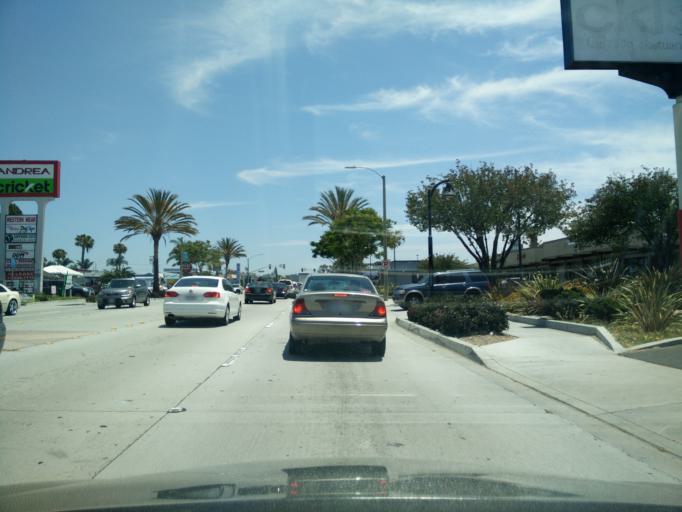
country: US
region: California
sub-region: San Diego County
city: Chula Vista
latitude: 32.6304
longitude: -117.0913
